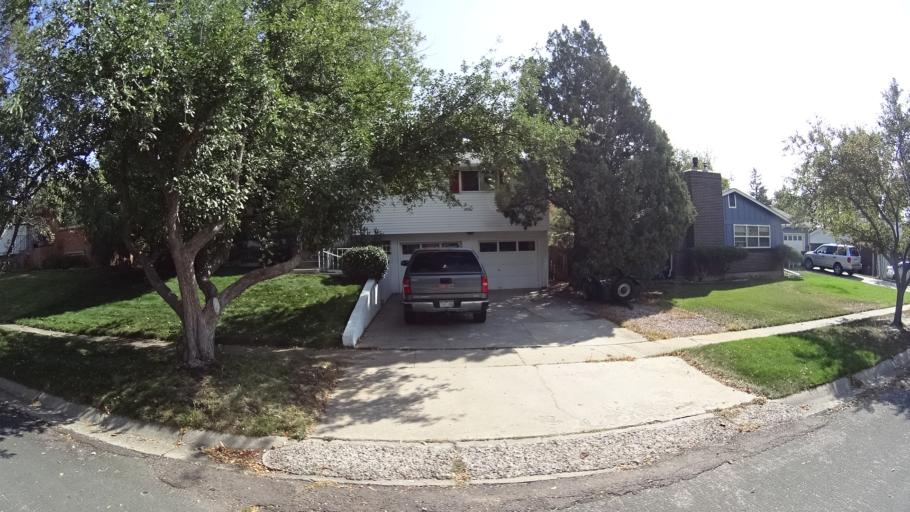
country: US
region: Colorado
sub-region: El Paso County
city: Colorado Springs
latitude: 38.8632
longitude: -104.7649
